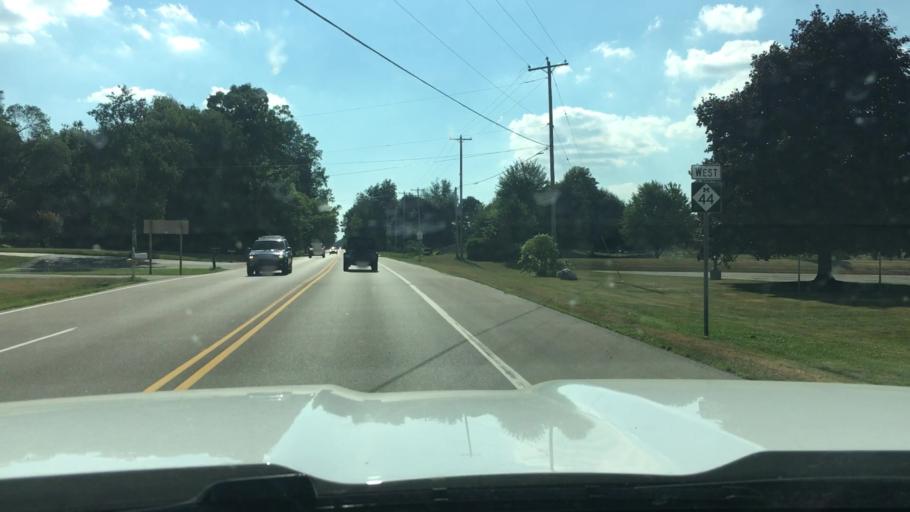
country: US
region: Michigan
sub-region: Kent County
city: Rockford
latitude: 43.0865
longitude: -85.4711
